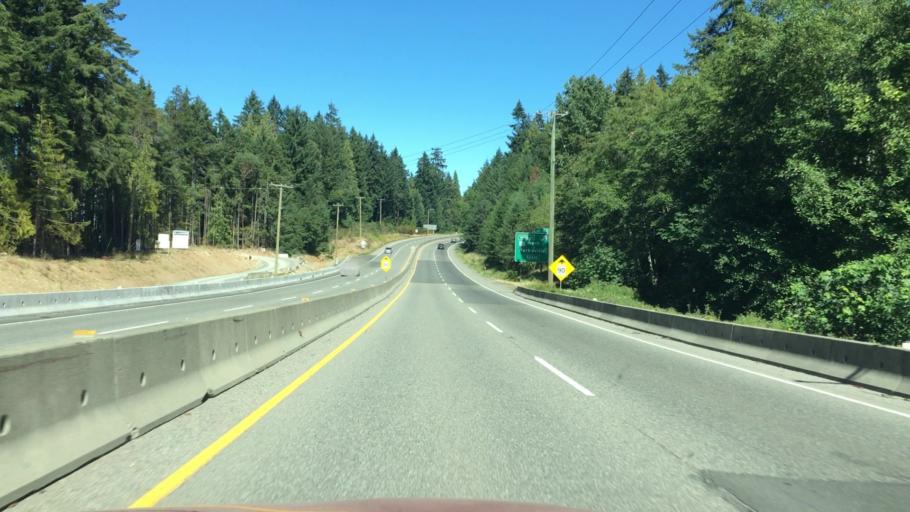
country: CA
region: British Columbia
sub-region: Regional District of Nanaimo
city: Parksville
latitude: 49.3010
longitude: -124.2719
